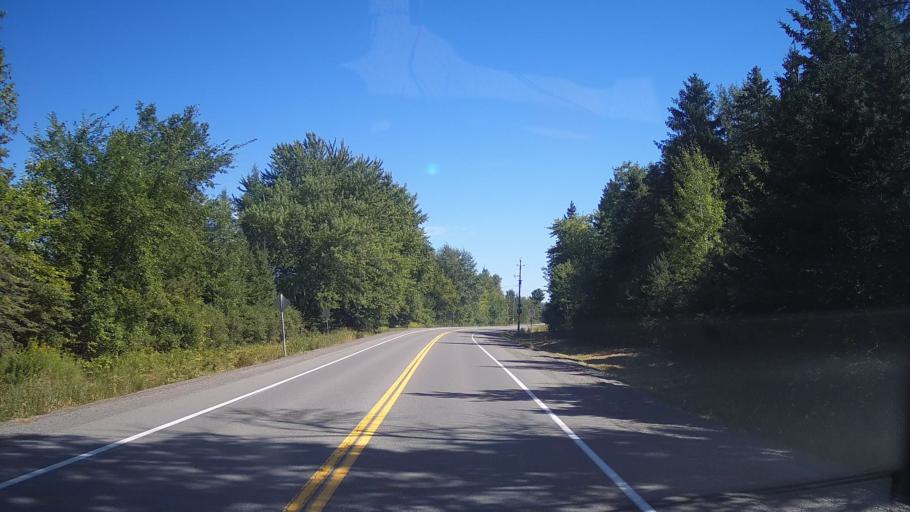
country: CA
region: Ontario
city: Bells Corners
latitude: 45.0619
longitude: -75.6698
